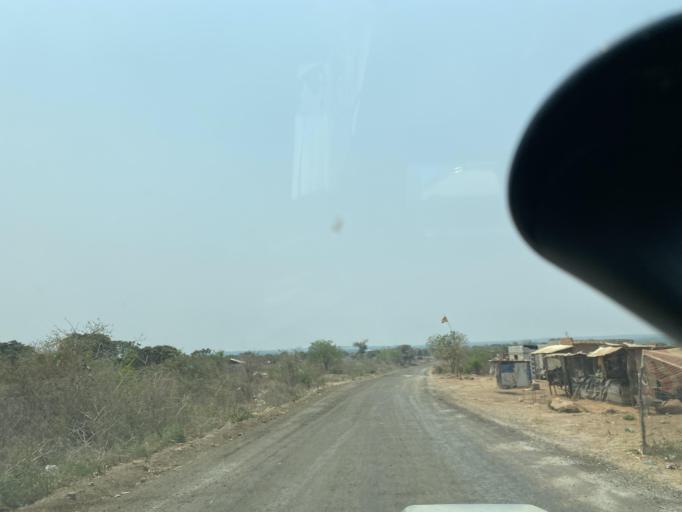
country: ZM
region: Lusaka
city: Lusaka
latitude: -15.5419
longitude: 28.4462
